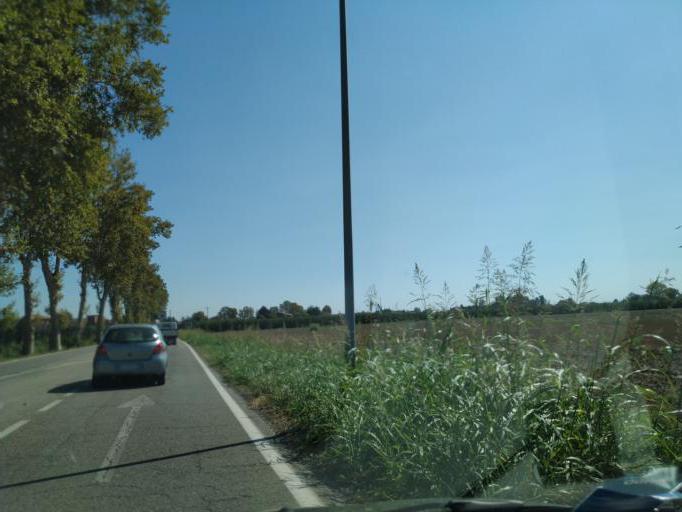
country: IT
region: Emilia-Romagna
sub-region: Provincia di Ferrara
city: La Saletta-Tamara
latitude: 44.8811
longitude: 11.7408
